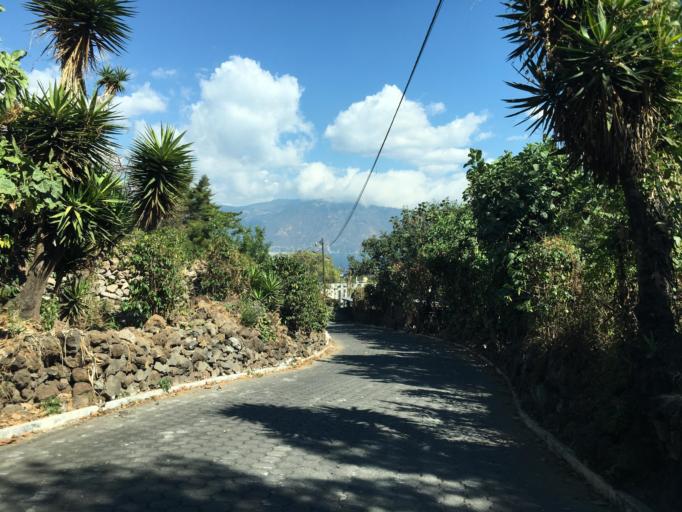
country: GT
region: Solola
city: Santa Catarina Palopo
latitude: 14.6691
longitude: -91.1689
